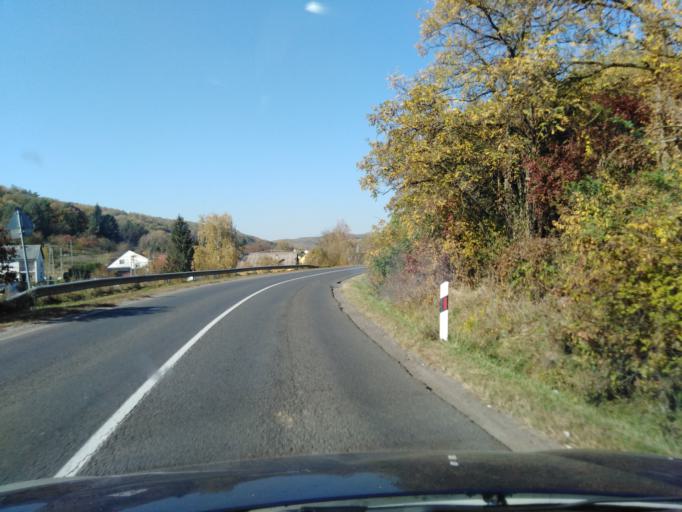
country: HU
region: Nograd
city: Salgotarjan
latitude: 48.1246
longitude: 19.7687
